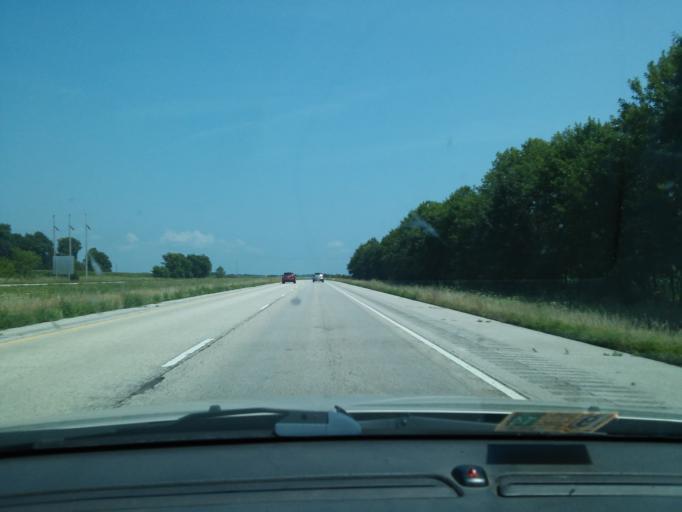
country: US
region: Illinois
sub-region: Sangamon County
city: New Berlin
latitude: 39.7368
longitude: -90.0175
